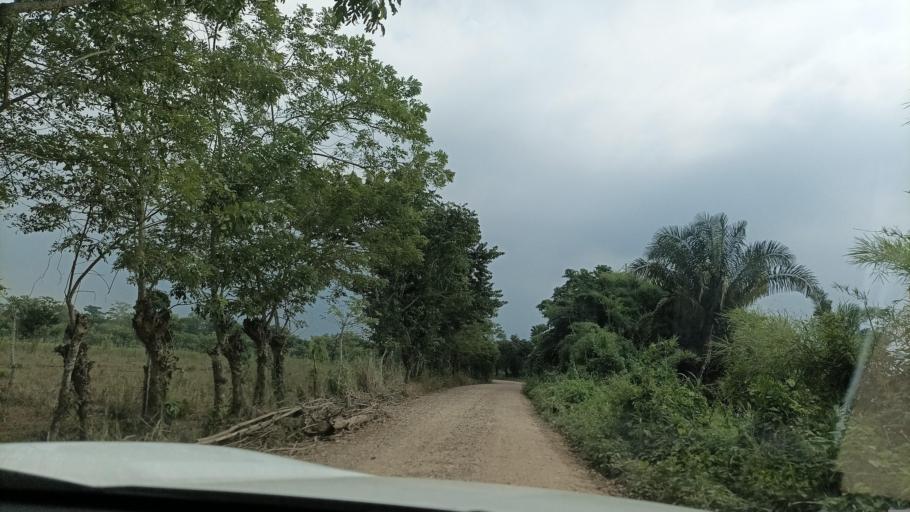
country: MX
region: Veracruz
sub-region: Moloacan
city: Cuichapa
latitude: 17.5826
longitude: -94.2121
